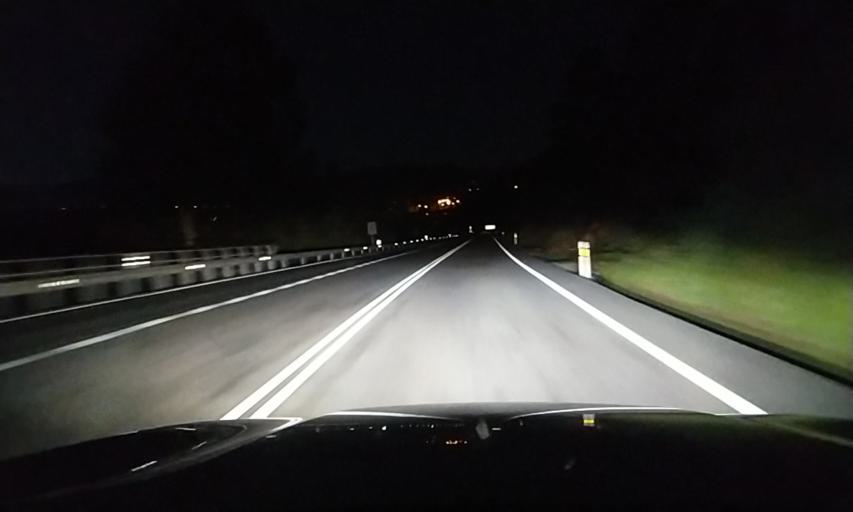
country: ES
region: Galicia
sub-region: Provincia de Ourense
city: Verin
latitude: 41.9576
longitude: -7.5019
